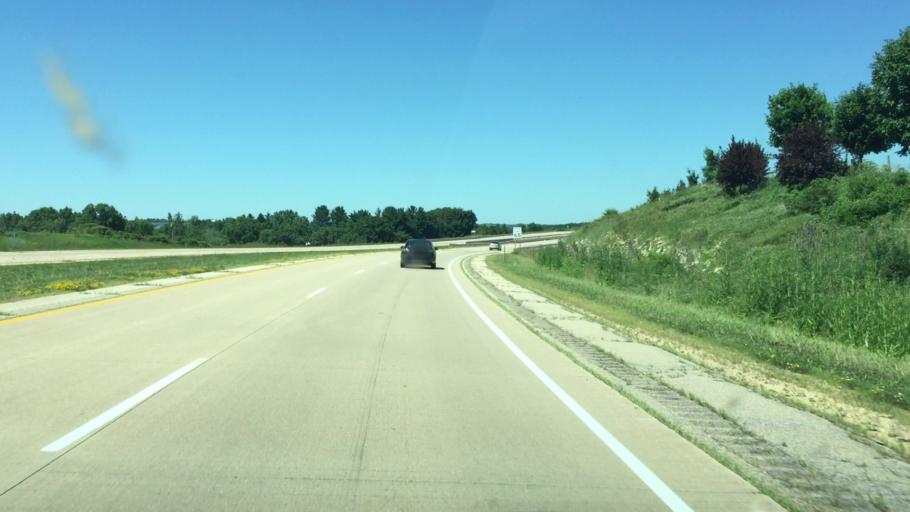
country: US
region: Wisconsin
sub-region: Iowa County
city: Mineral Point
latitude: 42.8591
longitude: -90.2031
